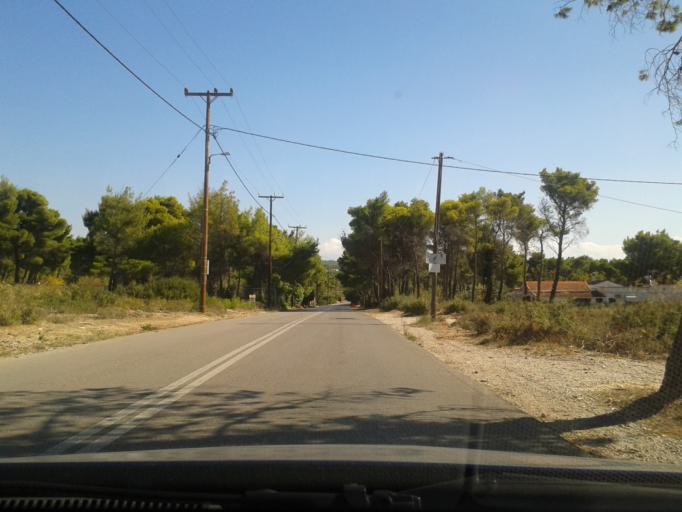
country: GR
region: Attica
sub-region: Nomarchia Anatolikis Attikis
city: Thrakomakedones
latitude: 38.1311
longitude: 23.7692
